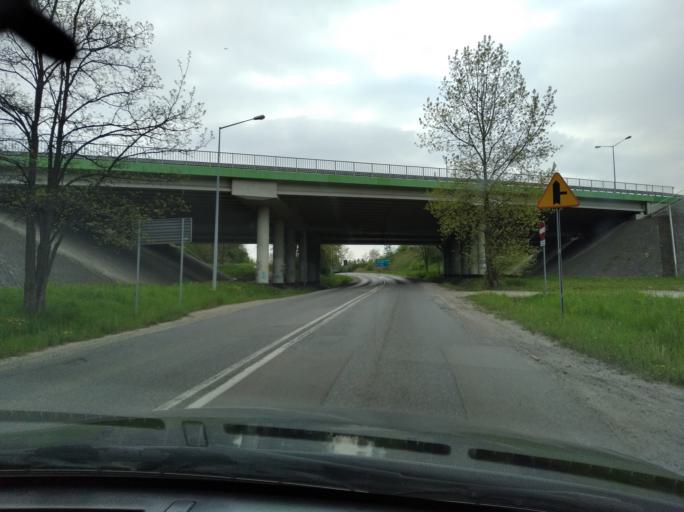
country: PL
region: Lesser Poland Voivodeship
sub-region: Powiat tarnowski
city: Tarnowiec
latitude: 49.9940
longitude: 20.9852
